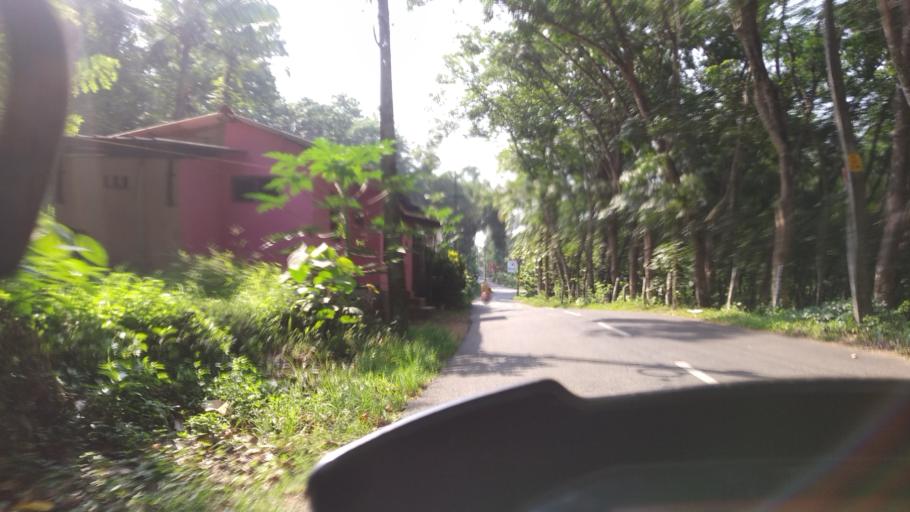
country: IN
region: Kerala
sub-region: Kottayam
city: Palackattumala
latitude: 9.8033
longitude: 76.5769
